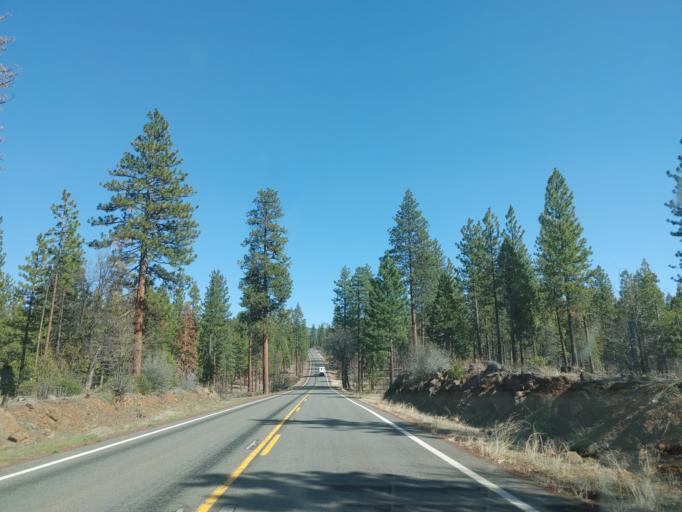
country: US
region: California
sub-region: Shasta County
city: Burney
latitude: 40.7350
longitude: -121.4513
